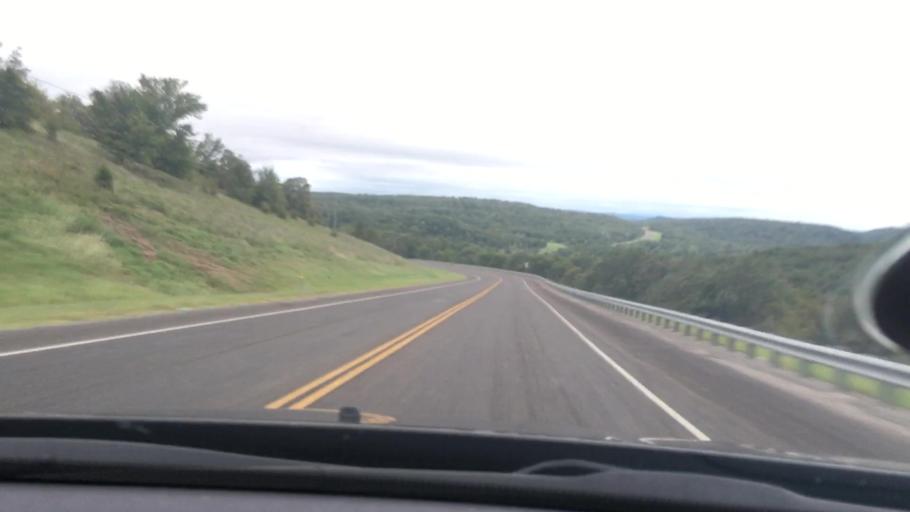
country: US
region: Oklahoma
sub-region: Sequoyah County
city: Vian
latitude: 35.5480
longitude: -94.9698
